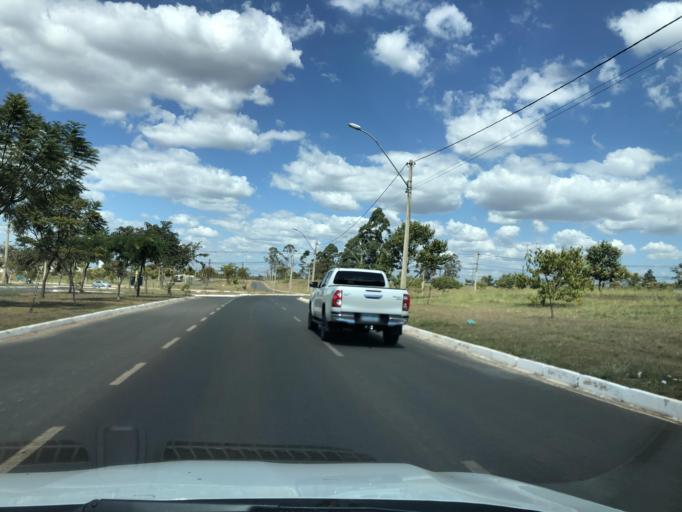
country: BR
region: Federal District
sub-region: Brasilia
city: Brasilia
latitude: -15.8870
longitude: -47.8190
